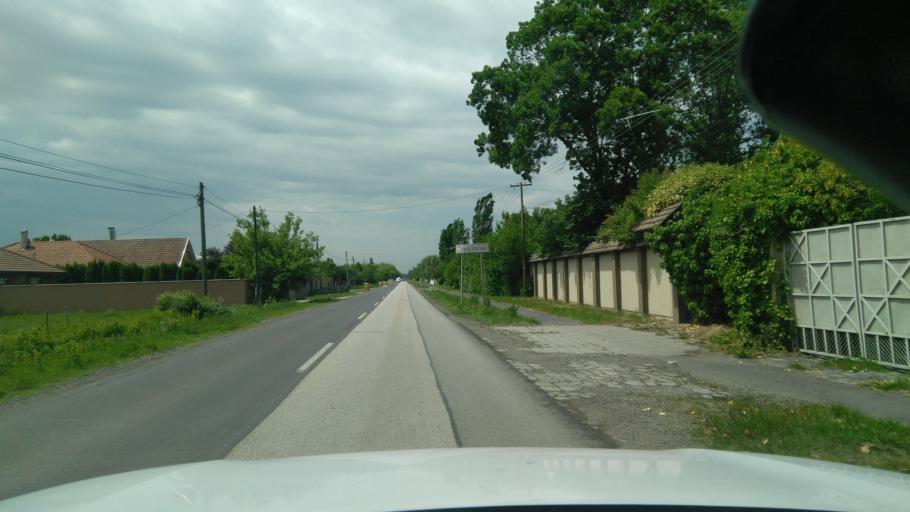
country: HU
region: Bekes
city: Bekescsaba
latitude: 46.6981
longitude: 21.1383
